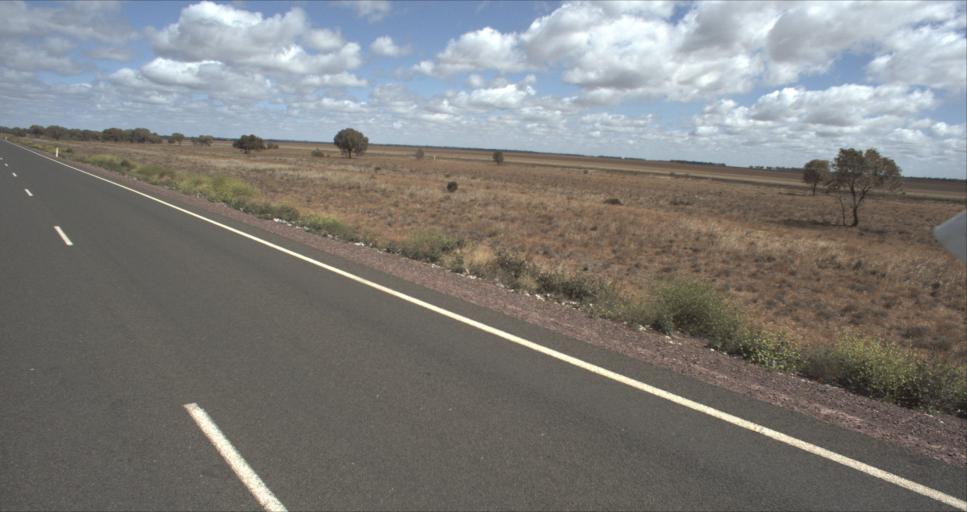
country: AU
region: New South Wales
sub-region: Murrumbidgee Shire
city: Darlington Point
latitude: -34.5752
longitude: 146.0719
